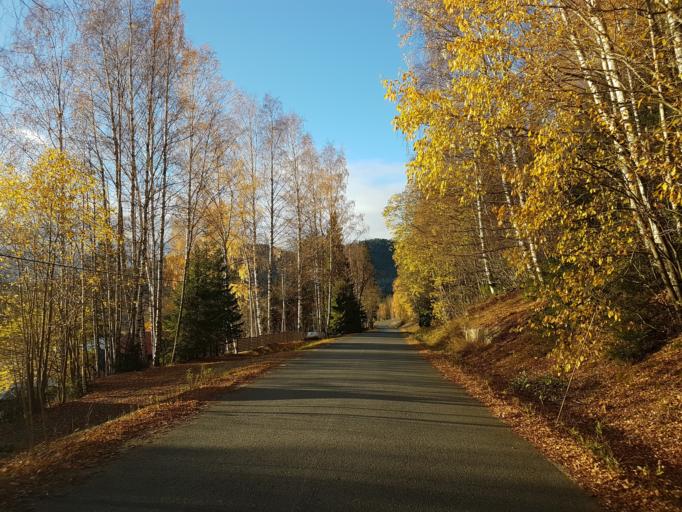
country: SE
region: Vaesternorrland
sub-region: Kramfors Kommun
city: Nordingra
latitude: 63.0649
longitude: 18.3750
